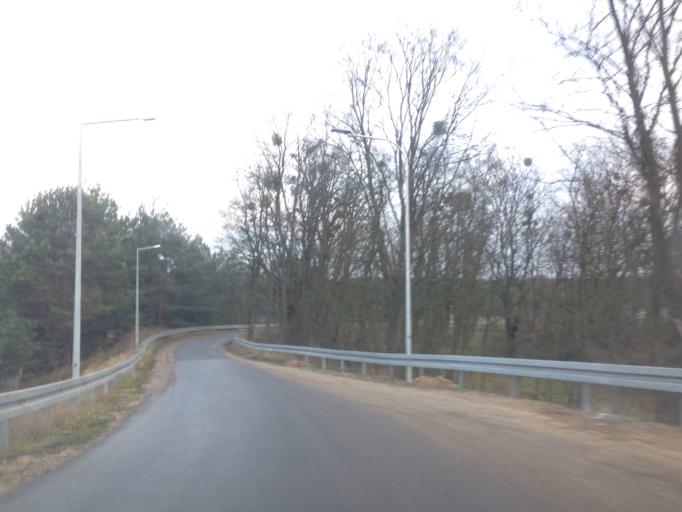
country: PL
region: Kujawsko-Pomorskie
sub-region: Powiat torunski
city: Wielka Nieszawka
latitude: 52.9924
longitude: 18.4454
